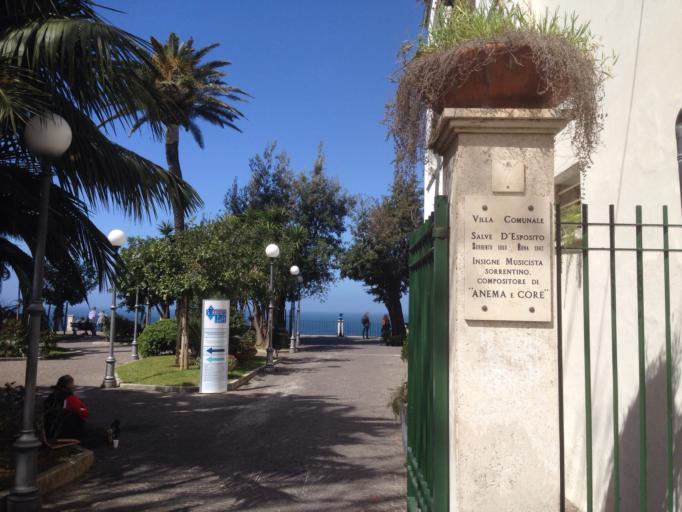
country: IT
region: Campania
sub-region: Provincia di Napoli
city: Sorrento
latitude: 40.6278
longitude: 14.3730
